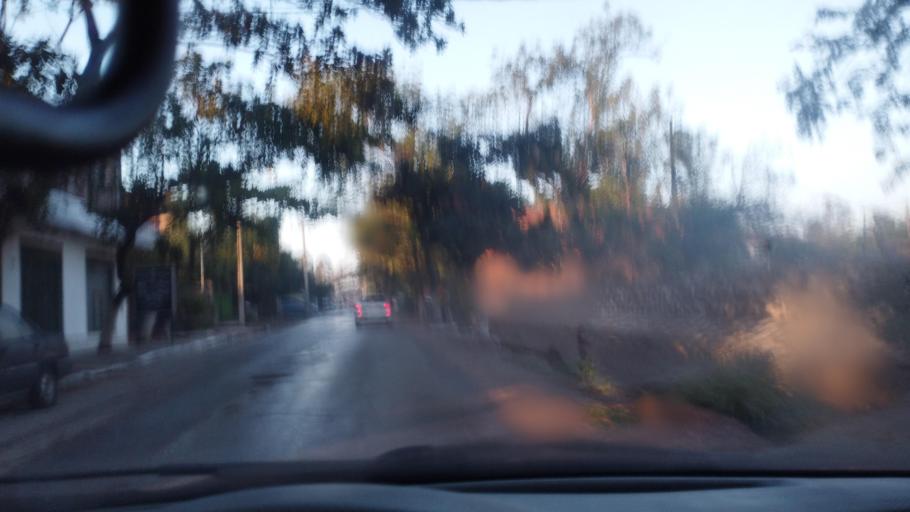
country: PY
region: Central
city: Fernando de la Mora
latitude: -25.2969
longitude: -57.5437
